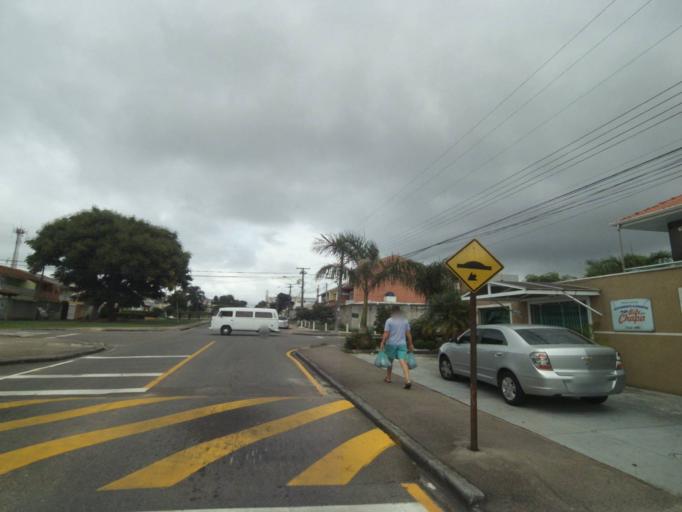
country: BR
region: Parana
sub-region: Pinhais
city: Pinhais
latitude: -25.4592
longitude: -49.2133
